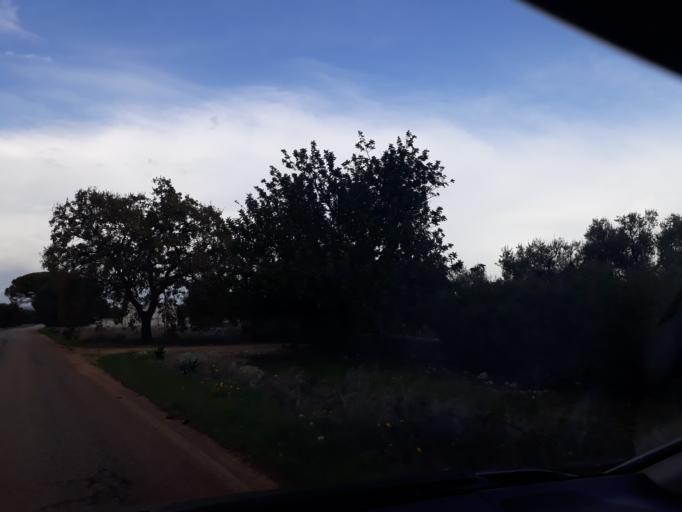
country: IT
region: Apulia
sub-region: Provincia di Brindisi
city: Pezze di Greco
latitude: 40.8059
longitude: 17.3916
